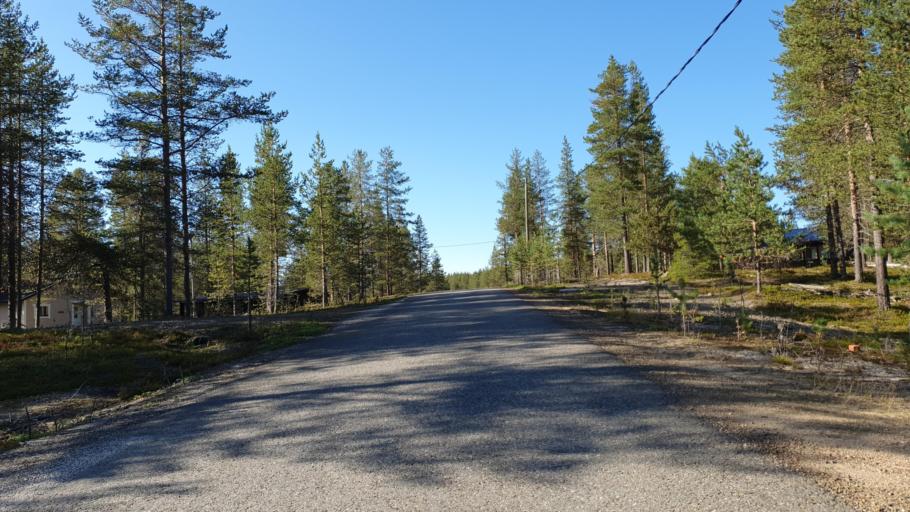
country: FI
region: Lapland
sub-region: Tunturi-Lappi
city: Kolari
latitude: 67.6071
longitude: 24.1958
